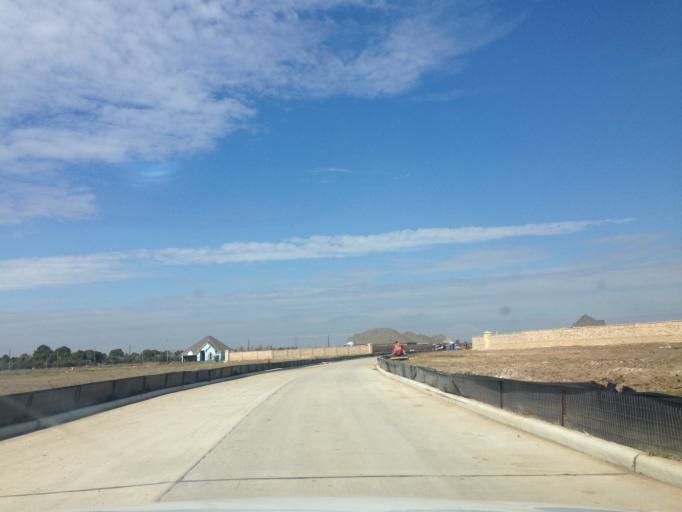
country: US
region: Texas
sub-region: Galveston County
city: Bacliff
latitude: 29.5180
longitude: -95.0119
